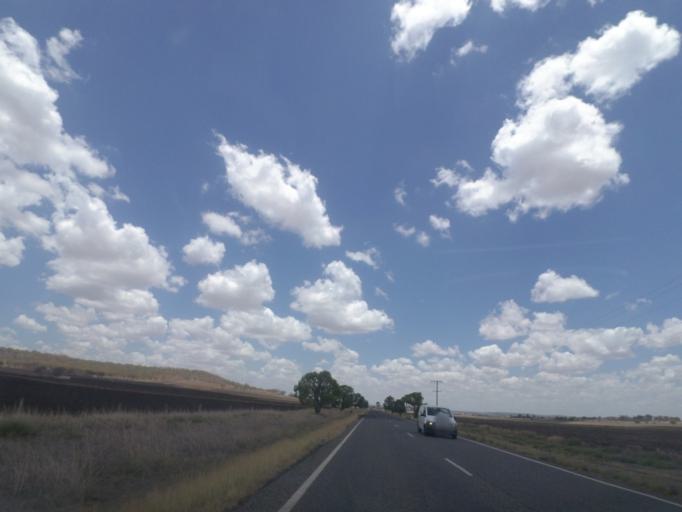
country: AU
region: Queensland
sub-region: Southern Downs
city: Warwick
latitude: -28.0078
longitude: 151.9900
